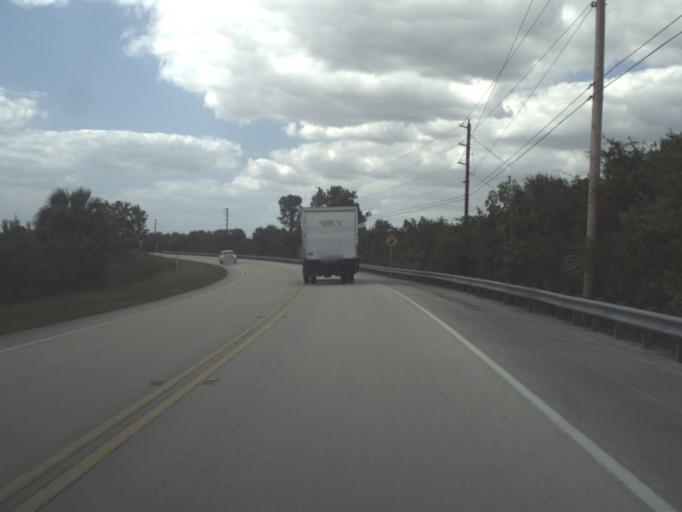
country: US
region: Florida
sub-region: Collier County
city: Lely Resort
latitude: 25.9857
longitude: -81.5680
